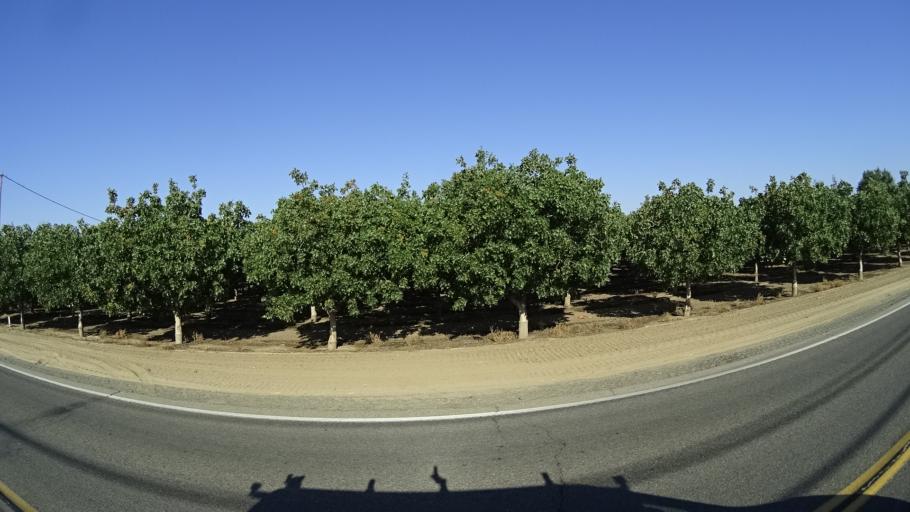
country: US
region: California
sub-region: Kings County
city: Armona
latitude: 36.3580
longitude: -119.7090
